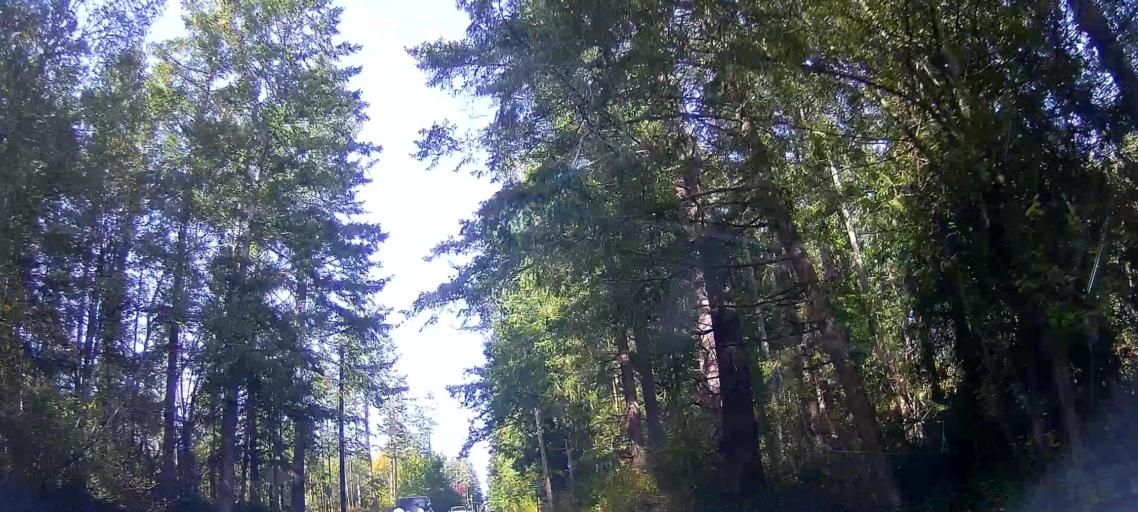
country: US
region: Washington
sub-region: Island County
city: Camano
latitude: 48.2166
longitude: -122.4560
